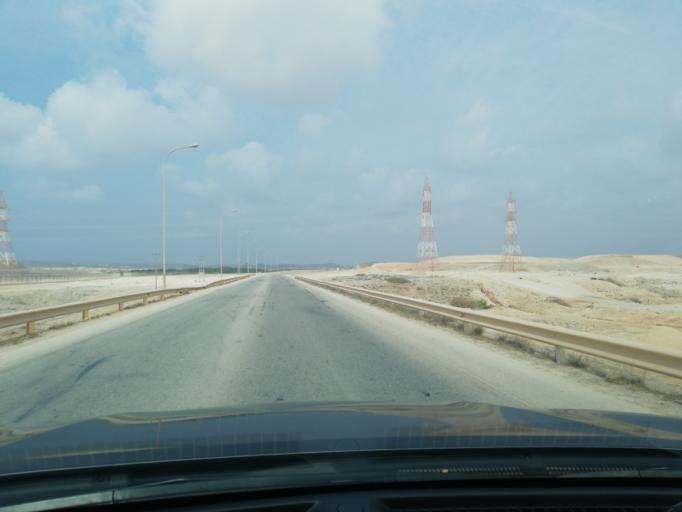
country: OM
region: Zufar
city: Salalah
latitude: 16.9474
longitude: 53.9612
